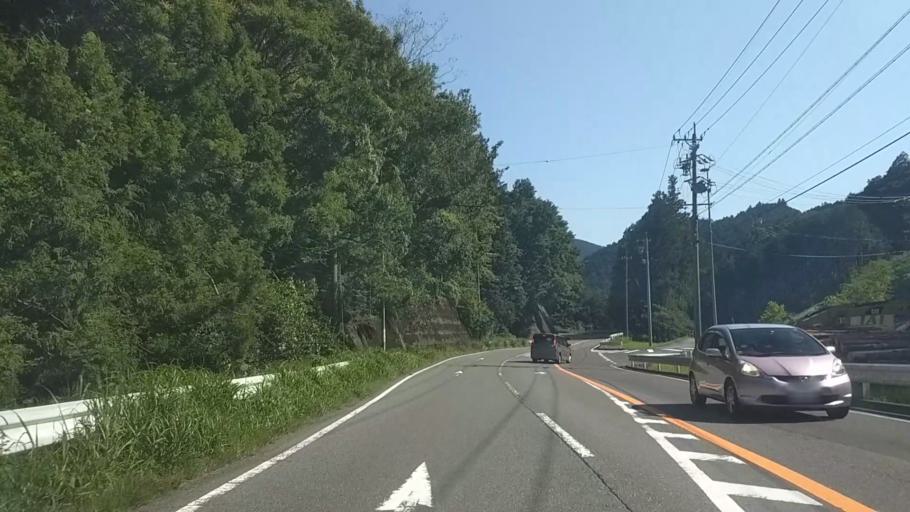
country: JP
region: Shizuoka
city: Fujinomiya
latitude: 35.1841
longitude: 138.5281
